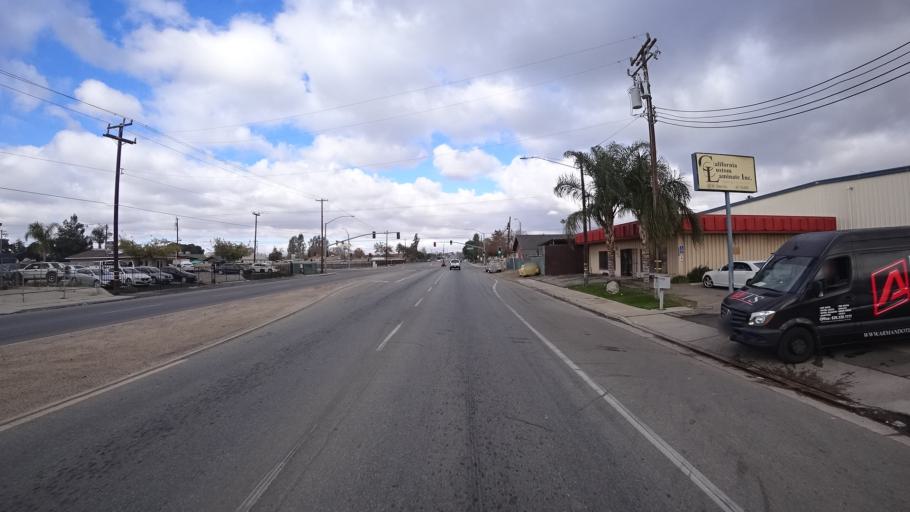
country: US
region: California
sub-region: Kern County
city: Bakersfield
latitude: 35.3606
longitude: -118.9674
